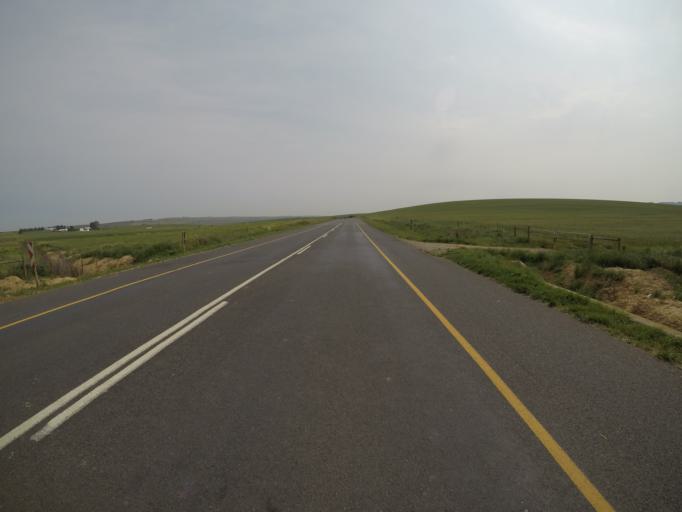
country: ZA
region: Western Cape
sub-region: West Coast District Municipality
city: Malmesbury
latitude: -33.4570
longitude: 18.7833
